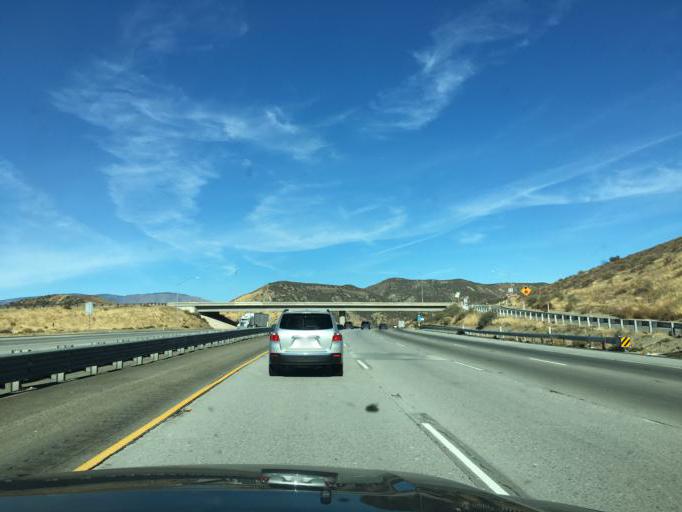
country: US
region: California
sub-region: Kern County
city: Lebec
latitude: 34.6652
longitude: -118.7621
